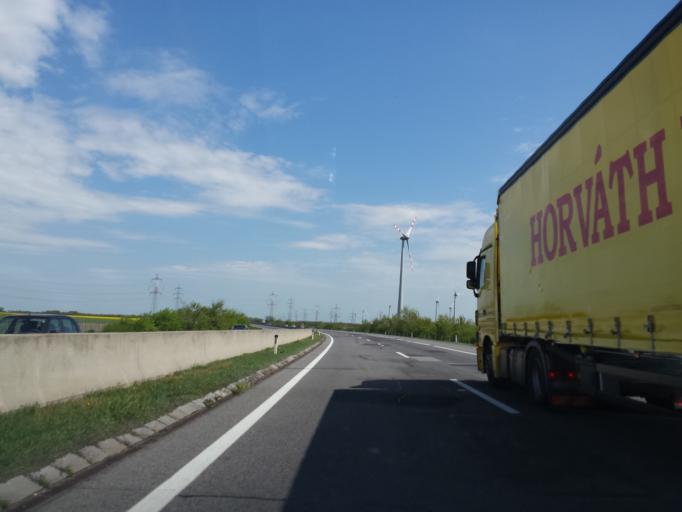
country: AT
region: Burgenland
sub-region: Politischer Bezirk Neusiedl am See
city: Nickelsdorf
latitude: 47.9242
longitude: 17.0134
